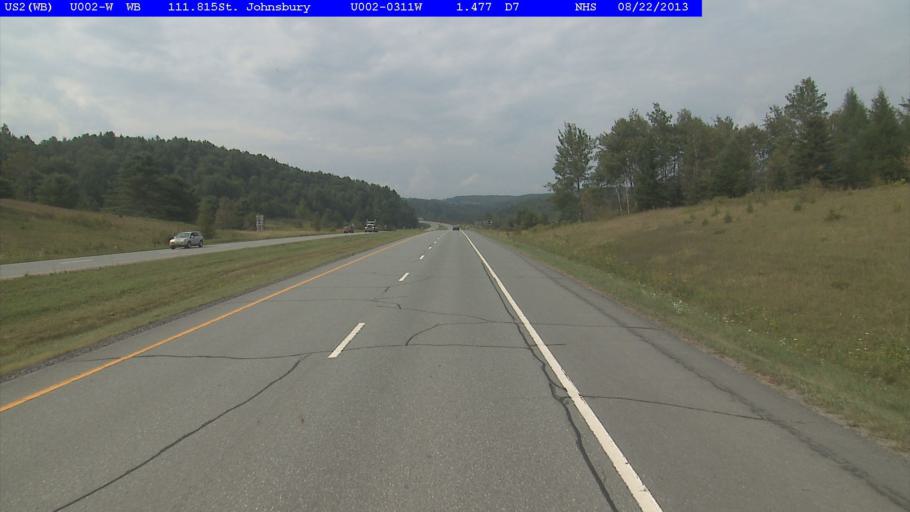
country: US
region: Vermont
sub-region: Caledonia County
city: St Johnsbury
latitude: 44.4336
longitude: -72.0405
